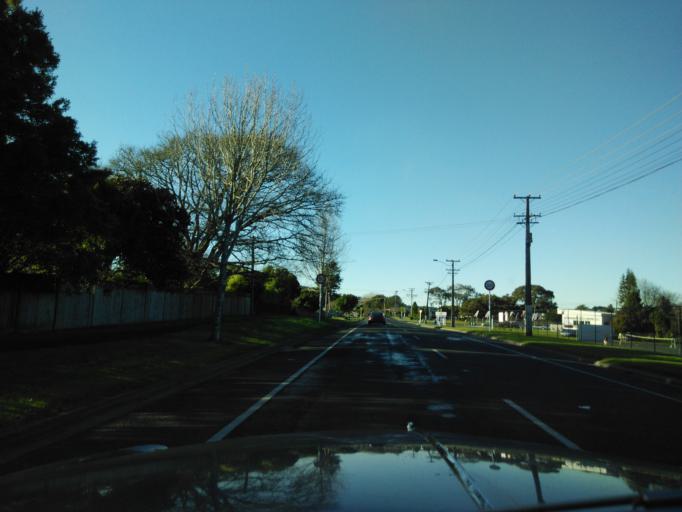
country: NZ
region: Auckland
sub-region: Auckland
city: Rosebank
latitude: -36.7596
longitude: 174.5902
